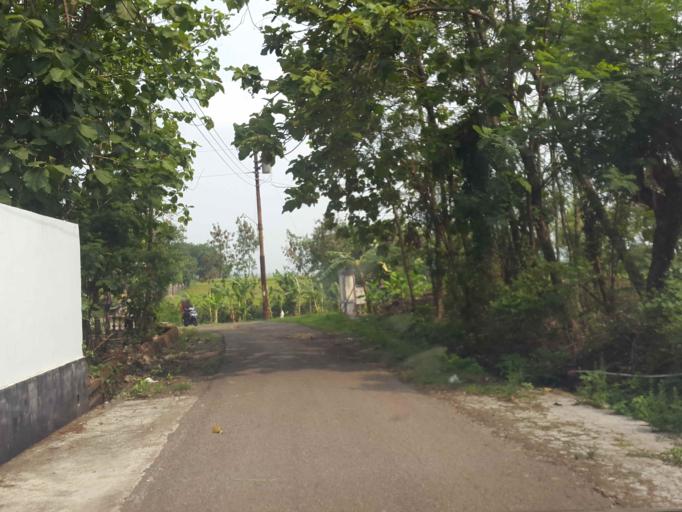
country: ID
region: Central Java
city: Jaten
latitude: -7.5130
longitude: 110.8895
